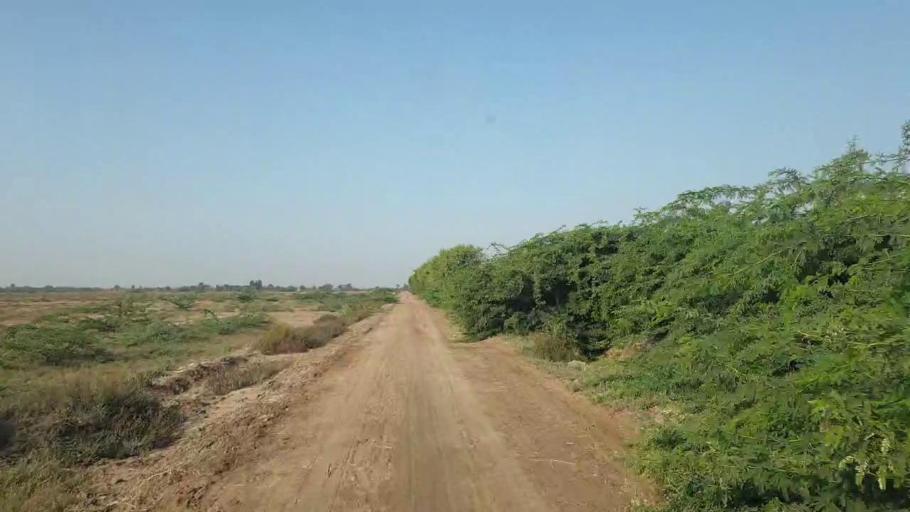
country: PK
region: Sindh
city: Badin
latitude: 24.4540
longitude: 68.7326
